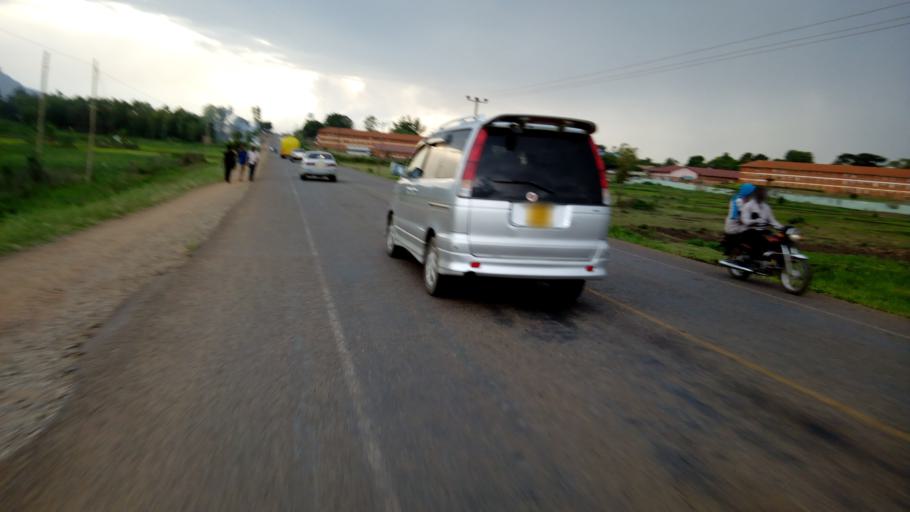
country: UG
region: Eastern Region
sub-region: Mbale District
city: Mbale
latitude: 1.1050
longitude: 34.1735
